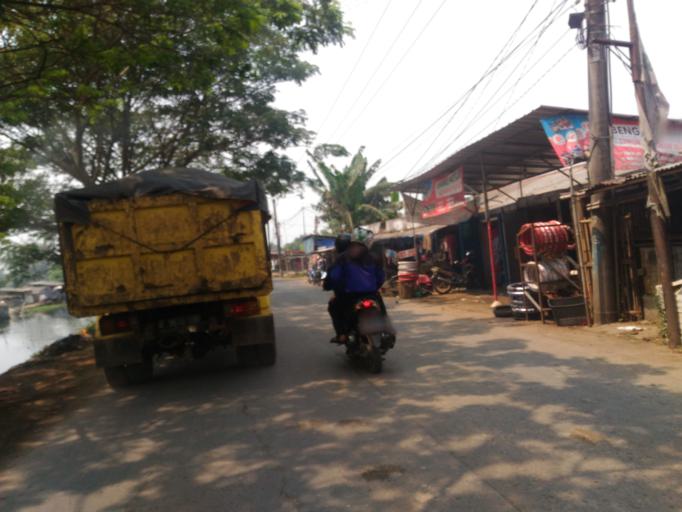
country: ID
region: West Java
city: Sepatan
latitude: -6.1467
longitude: 106.5648
